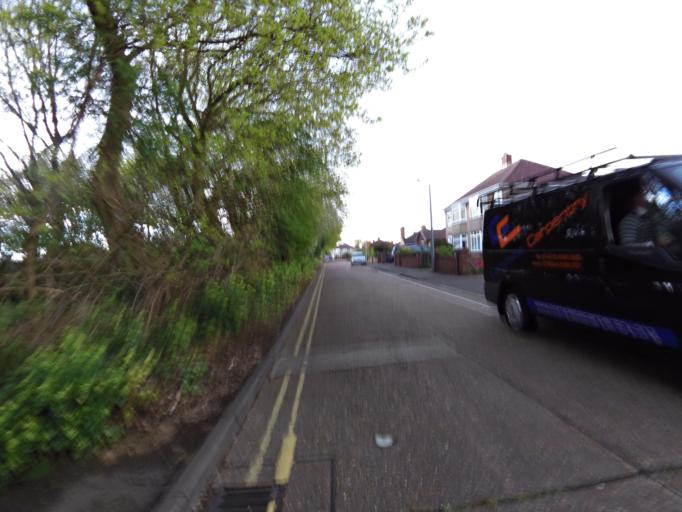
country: GB
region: England
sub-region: Suffolk
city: Kesgrave
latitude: 52.0574
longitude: 1.2040
